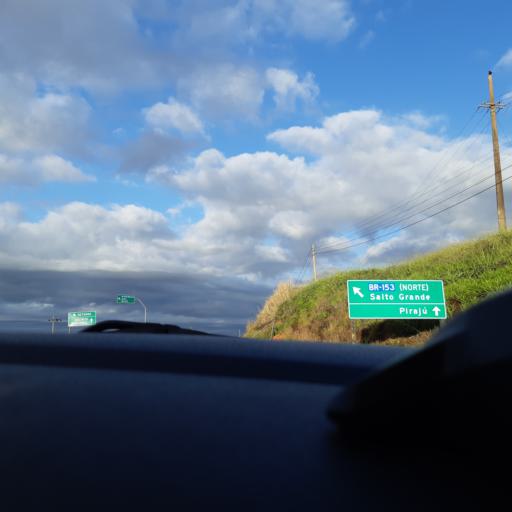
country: BR
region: Sao Paulo
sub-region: Ourinhos
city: Ourinhos
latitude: -22.9942
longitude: -49.8468
